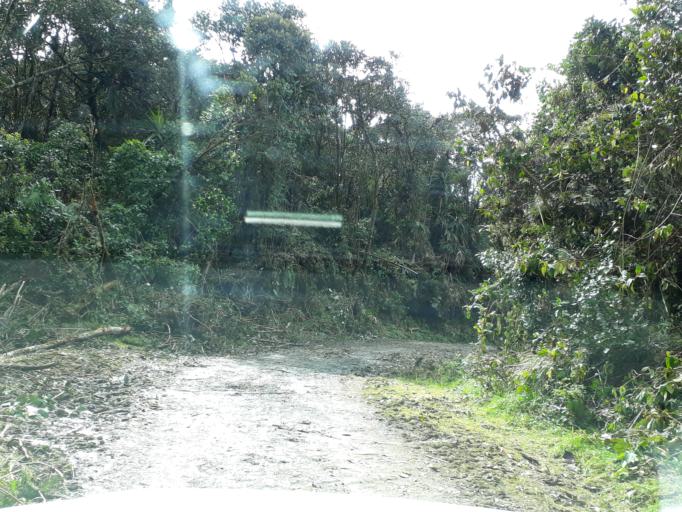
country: CO
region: Cundinamarca
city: Junin
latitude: 4.7928
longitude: -73.7792
